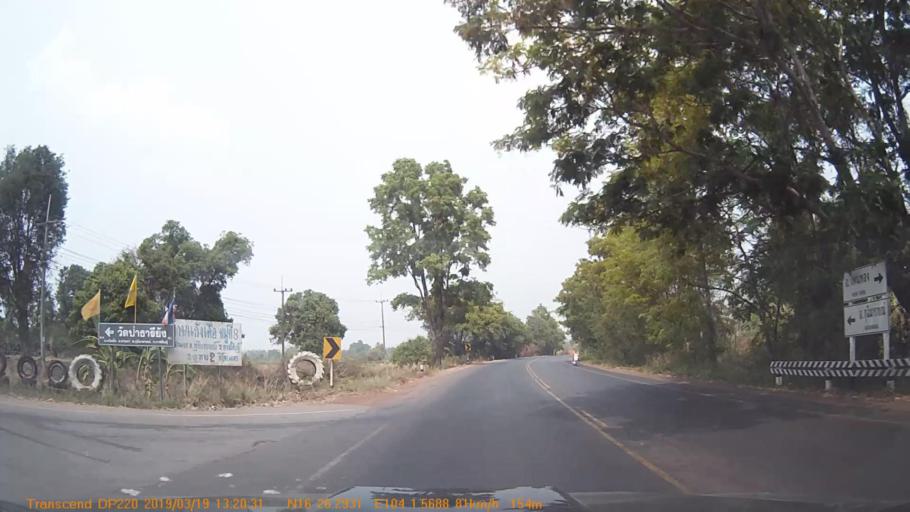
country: TH
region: Kalasin
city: Kuchinarai
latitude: 16.4385
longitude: 104.0263
